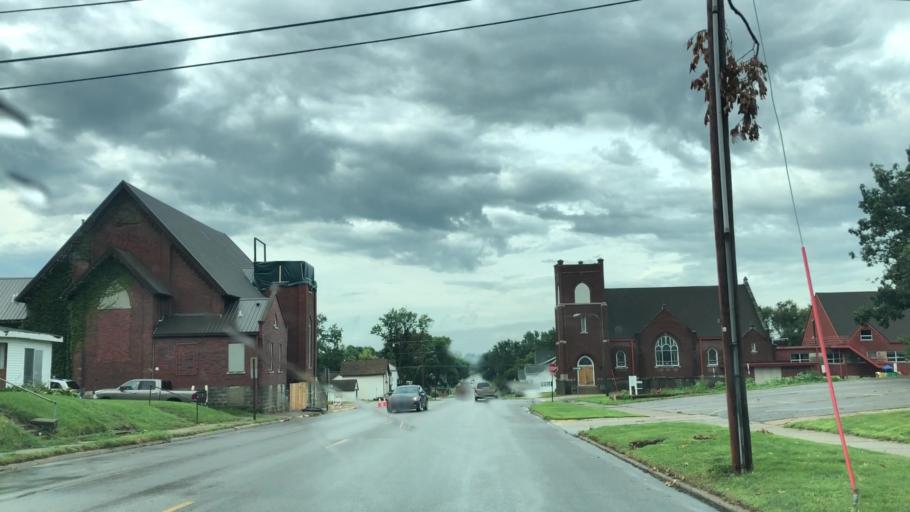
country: US
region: Iowa
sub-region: Marshall County
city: Marshalltown
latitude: 42.0486
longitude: -92.9179
